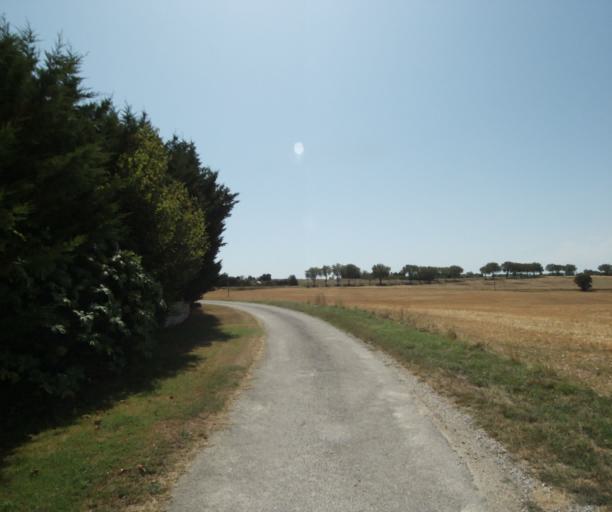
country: FR
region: Midi-Pyrenees
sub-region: Departement de la Haute-Garonne
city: Saint-Felix-Lauragais
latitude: 43.4620
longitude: 1.8501
